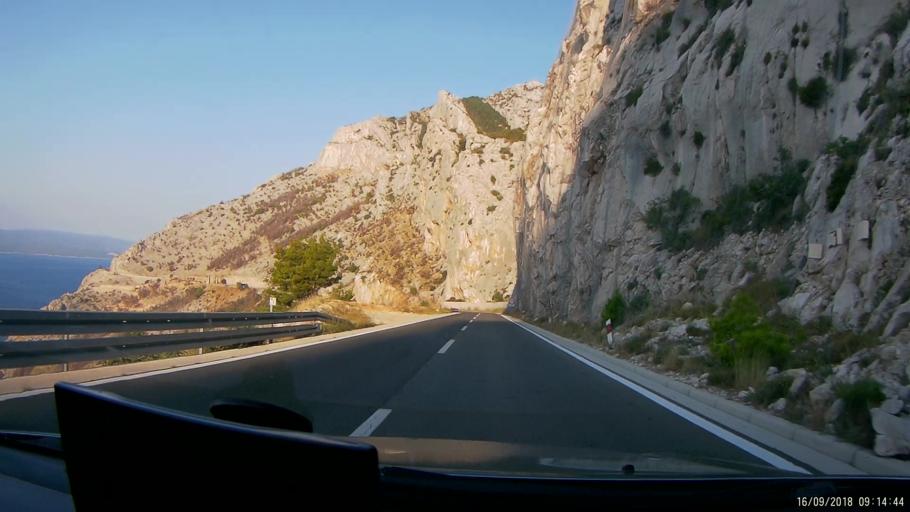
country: HR
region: Splitsko-Dalmatinska
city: Donja Brela
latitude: 43.4041
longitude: 16.8870
